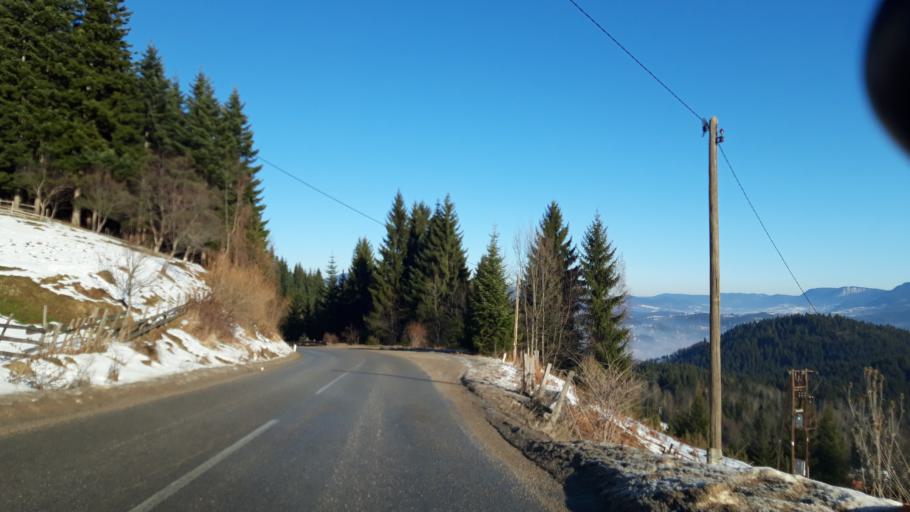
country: BA
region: Republika Srpska
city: Koran
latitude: 43.7938
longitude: 18.5557
